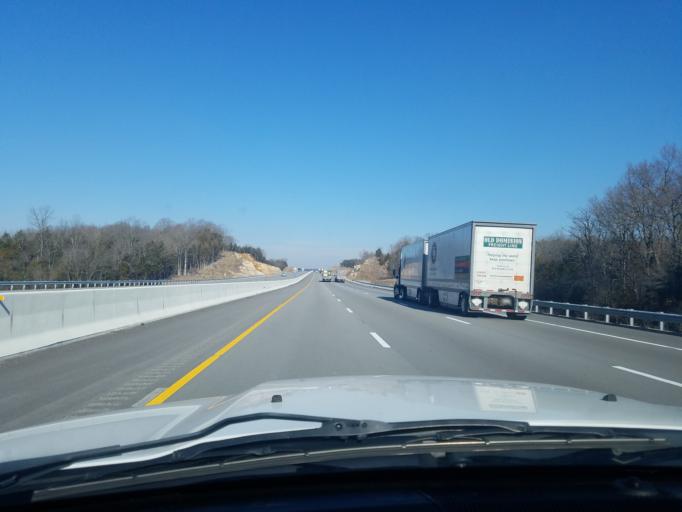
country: US
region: Kentucky
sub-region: Hart County
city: Munfordville
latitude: 37.4150
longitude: -85.8817
